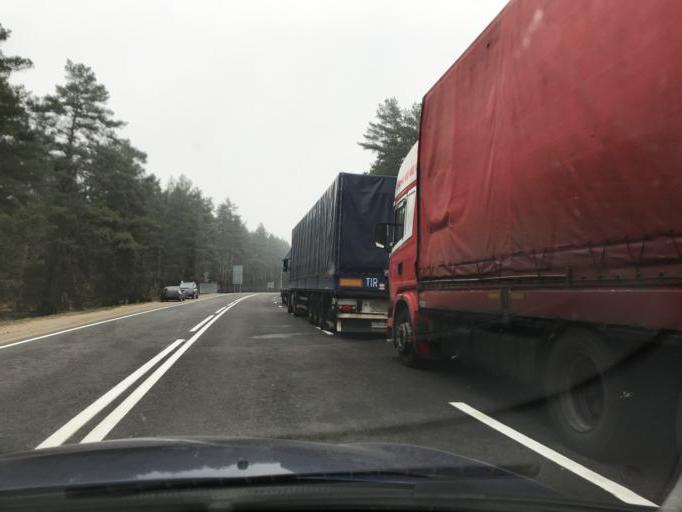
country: LT
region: Alytaus apskritis
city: Druskininkai
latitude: 53.9377
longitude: 23.9552
